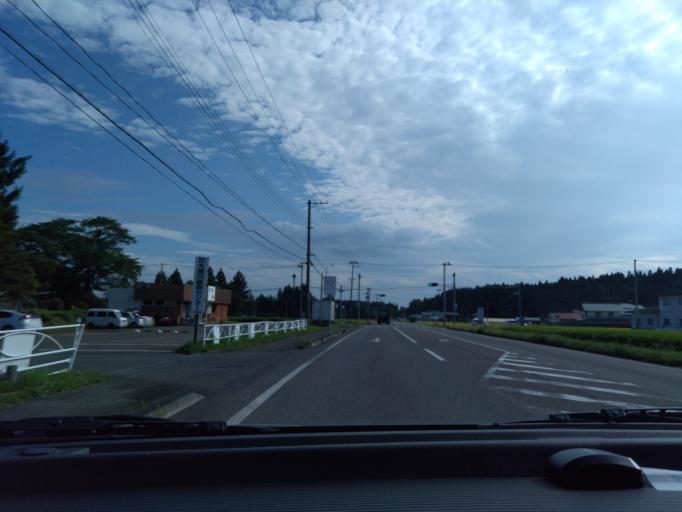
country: JP
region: Iwate
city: Hanamaki
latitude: 39.5001
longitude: 141.1128
